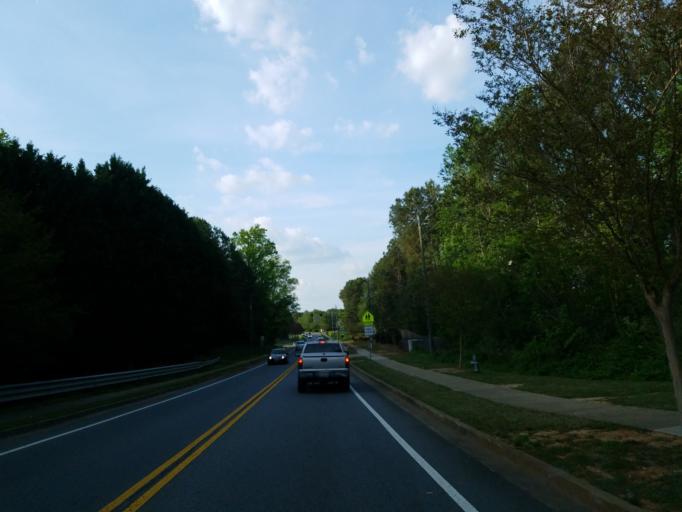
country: US
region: Georgia
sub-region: Fulton County
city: Roswell
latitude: 34.0682
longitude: -84.3608
